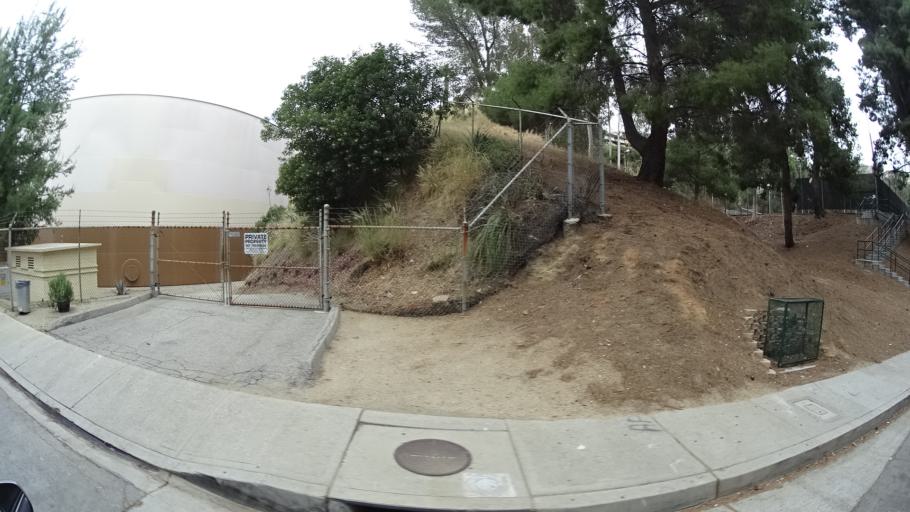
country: US
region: California
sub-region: Los Angeles County
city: Burbank
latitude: 34.2116
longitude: -118.3290
